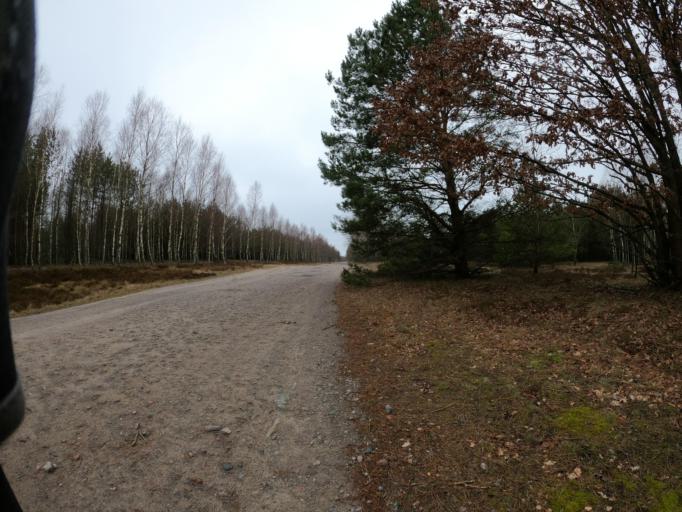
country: PL
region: West Pomeranian Voivodeship
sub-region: Powiat szczecinecki
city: Borne Sulinowo
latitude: 53.5398
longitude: 16.5803
